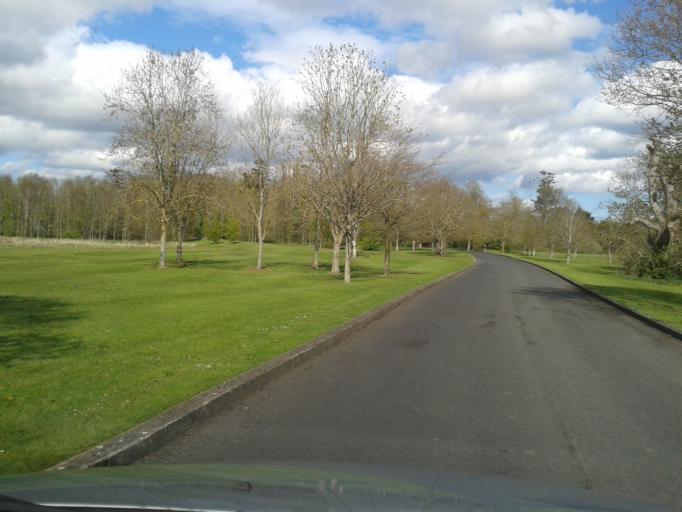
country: IE
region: Leinster
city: Donabate
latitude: 53.4838
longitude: -6.1762
